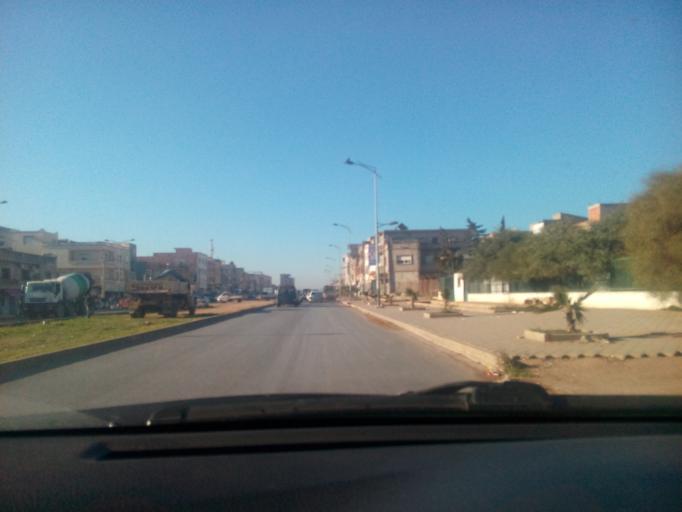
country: DZ
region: Oran
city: Bir el Djir
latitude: 35.7472
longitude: -0.5580
